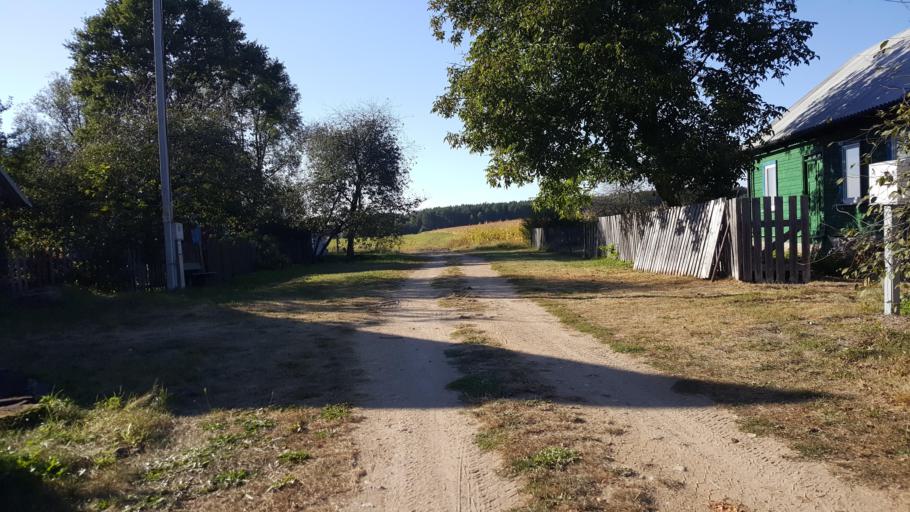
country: BY
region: Brest
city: Vysokaye
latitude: 52.3303
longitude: 23.2608
